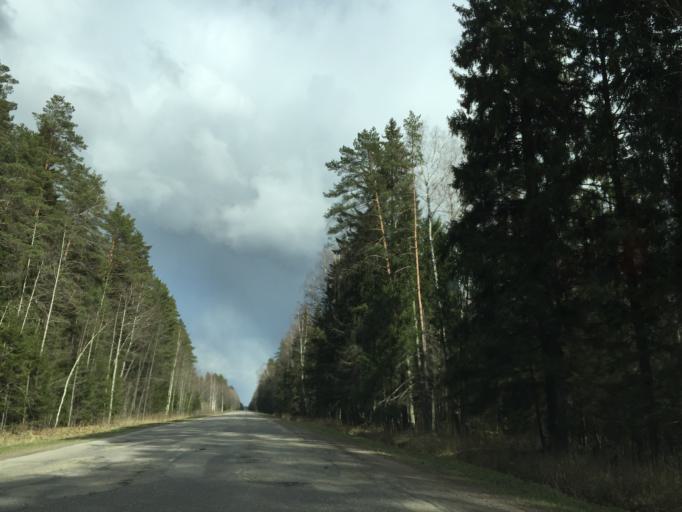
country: LV
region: Garkalne
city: Garkalne
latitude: 56.9470
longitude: 24.4707
